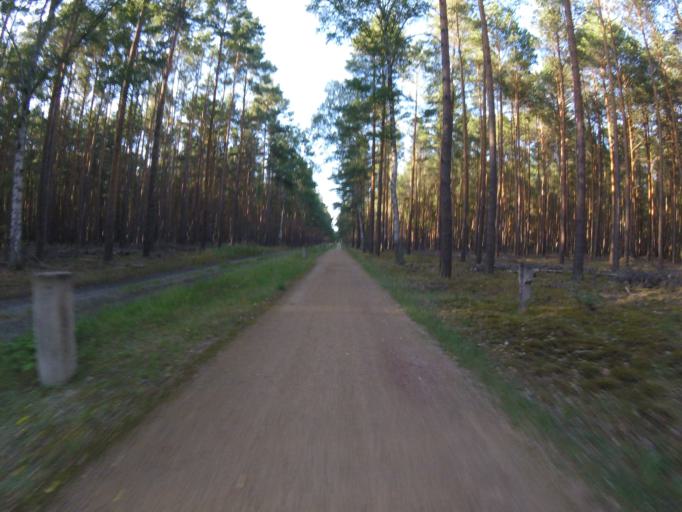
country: DE
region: Brandenburg
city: Munchehofe
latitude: 52.1982
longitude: 13.7650
